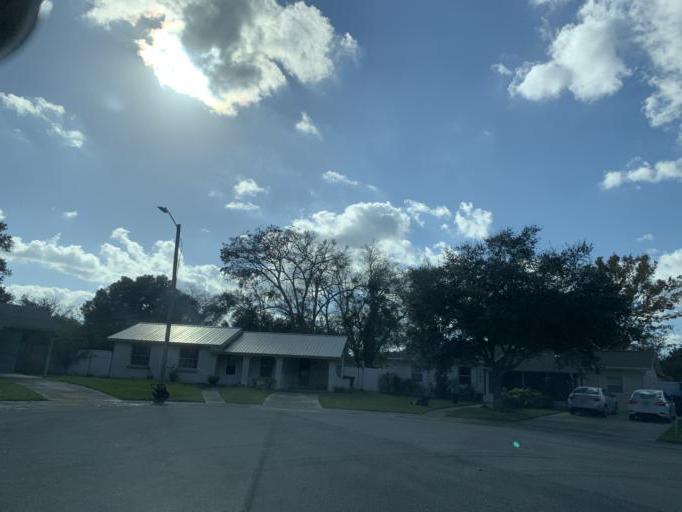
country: US
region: Florida
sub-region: Orange County
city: Eatonville
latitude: 28.6131
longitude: -81.3964
